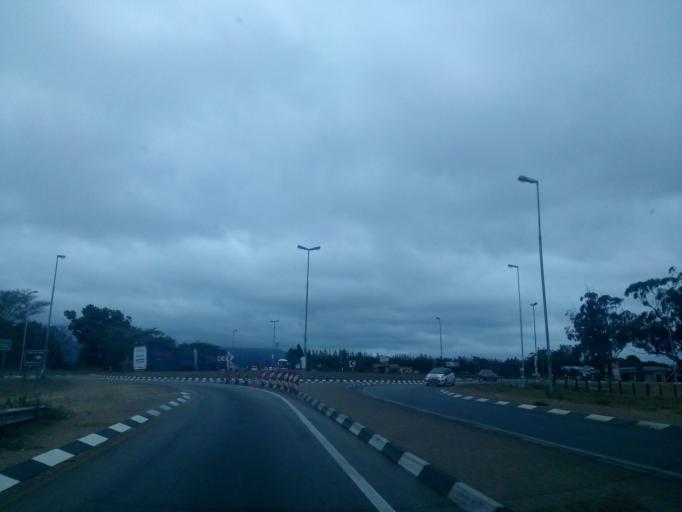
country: ZA
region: Limpopo
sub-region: Vhembe District Municipality
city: Louis Trichardt
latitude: -23.0789
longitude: 29.9085
